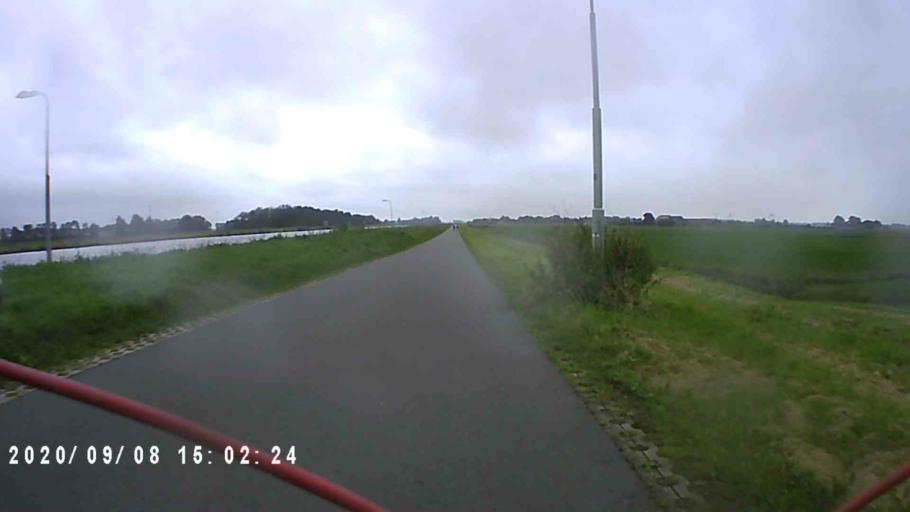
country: NL
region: Groningen
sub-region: Gemeente Slochteren
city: Slochteren
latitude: 53.2773
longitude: 6.7561
